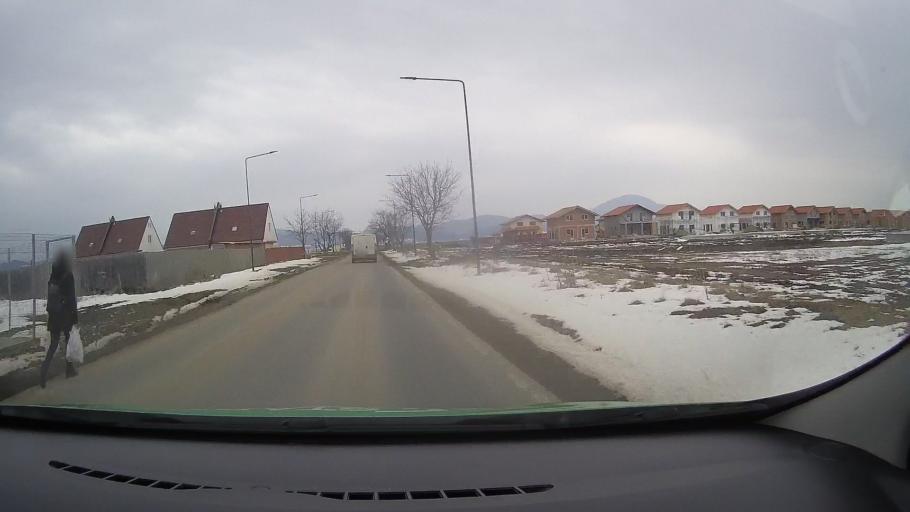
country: RO
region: Brasov
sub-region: Comuna Cristian
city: Cristian
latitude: 45.6291
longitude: 25.4667
